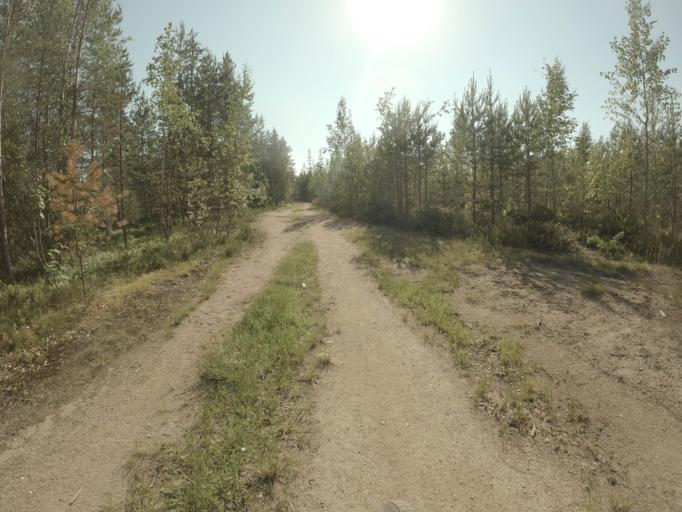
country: RU
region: Leningrad
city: Yakovlevo
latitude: 60.4548
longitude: 29.2647
